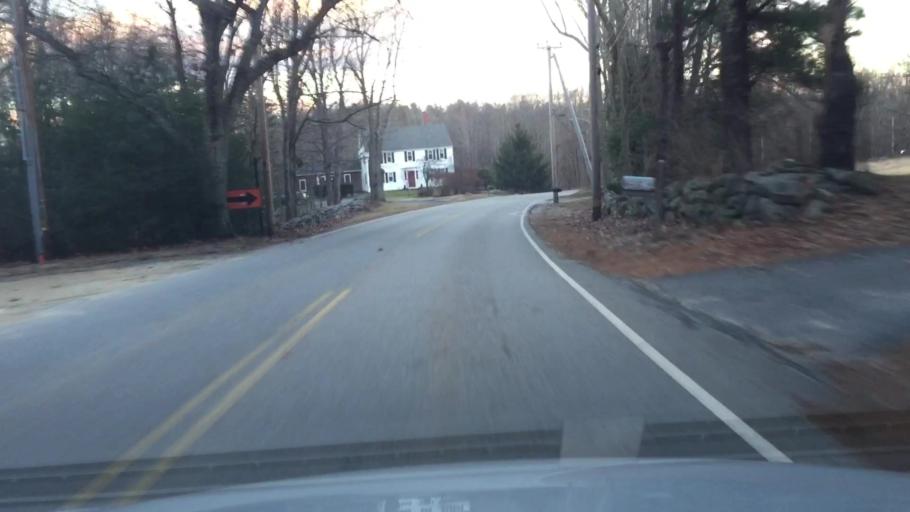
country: US
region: Massachusetts
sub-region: Worcester County
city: Princeton
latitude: 42.4444
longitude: -71.8372
